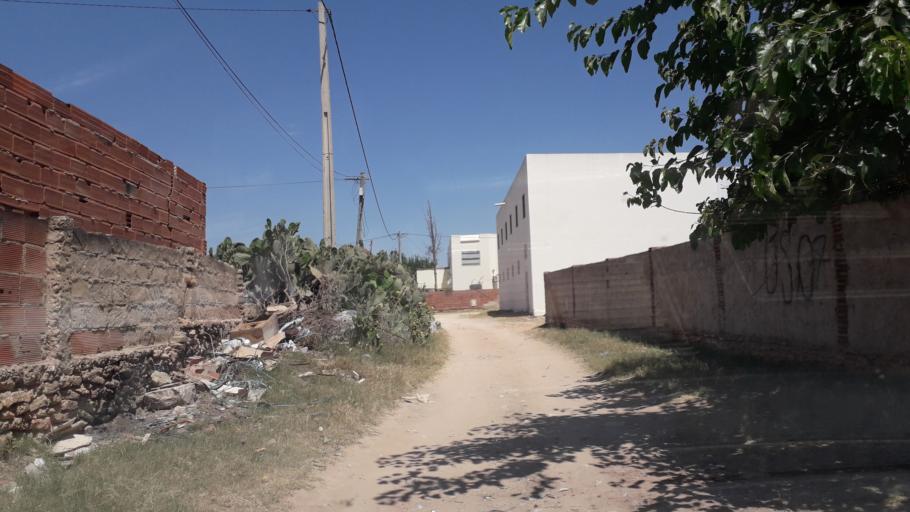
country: TN
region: Safaqis
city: Al Qarmadah
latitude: 34.8234
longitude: 10.7690
